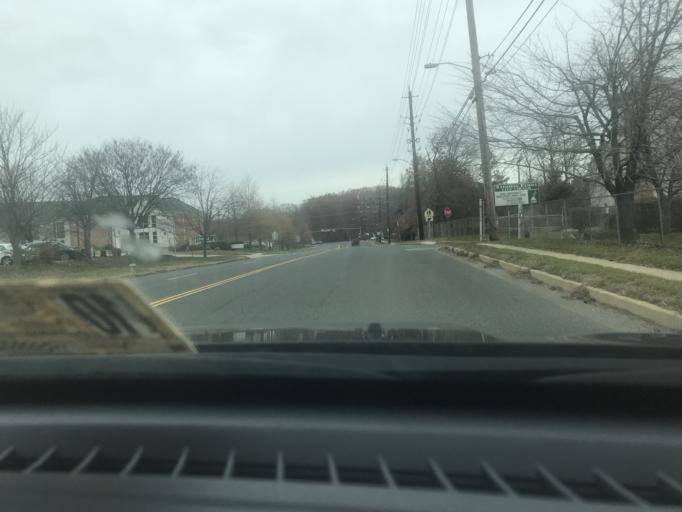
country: US
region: Maryland
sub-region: Prince George's County
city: Oxon Hill
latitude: 38.7984
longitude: -76.9784
